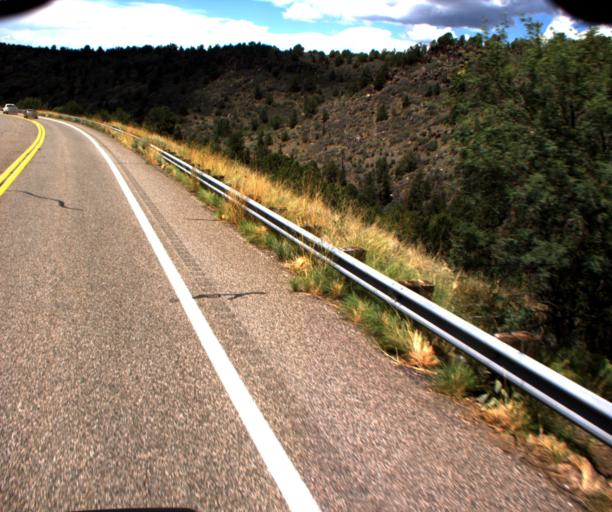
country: US
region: Arizona
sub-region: Yavapai County
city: Lake Montezuma
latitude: 34.5042
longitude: -111.6439
